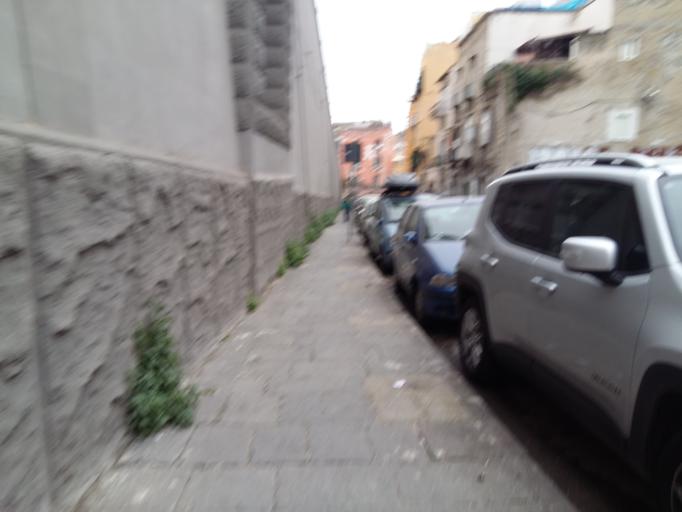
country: IT
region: Campania
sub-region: Provincia di Napoli
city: Napoli
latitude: 40.8537
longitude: 14.2440
